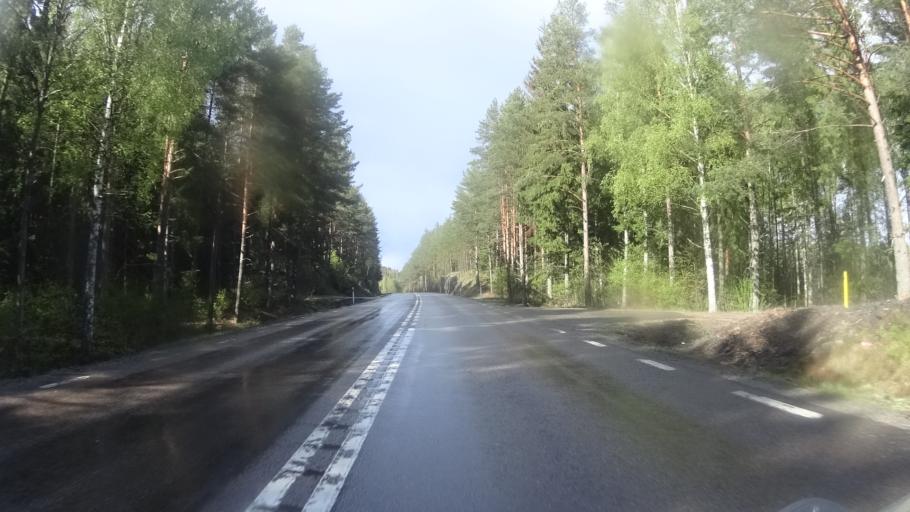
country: SE
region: OErebro
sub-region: Askersunds Kommun
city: Askersund
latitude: 58.7375
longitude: 14.7778
